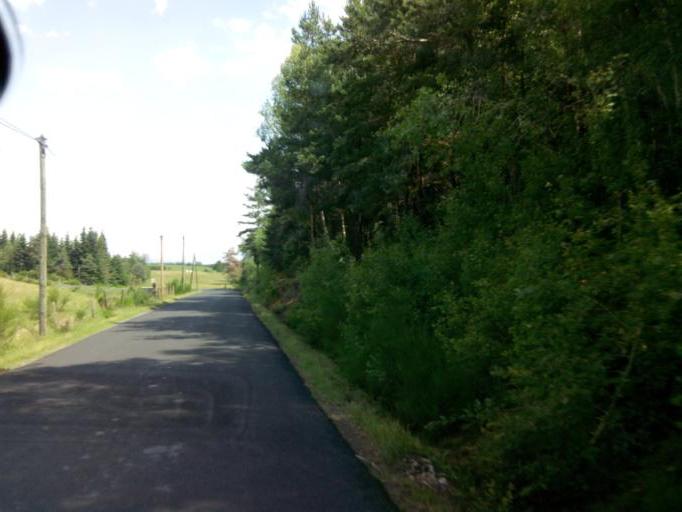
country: FR
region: Rhone-Alpes
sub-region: Departement de la Loire
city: Usson-en-Forez
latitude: 45.3659
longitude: 3.9604
